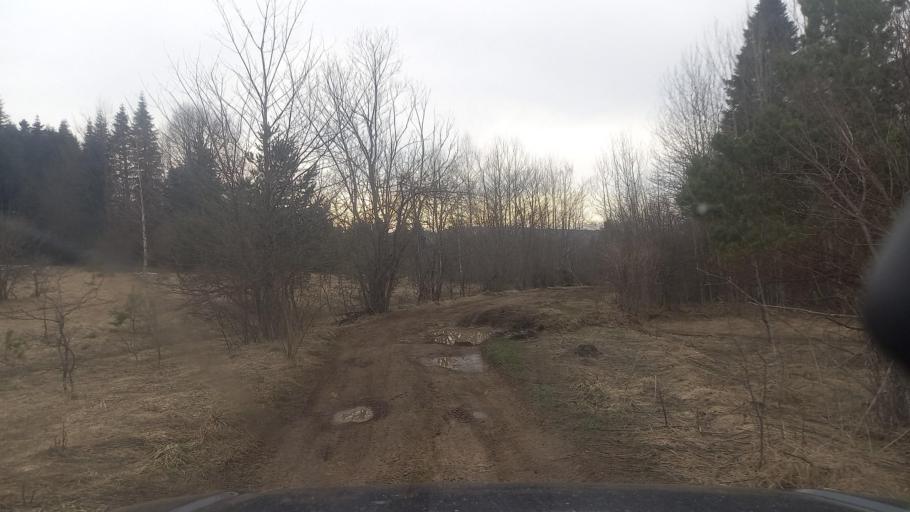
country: RU
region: Adygeya
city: Kamennomostskiy
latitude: 44.1649
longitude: 40.0182
